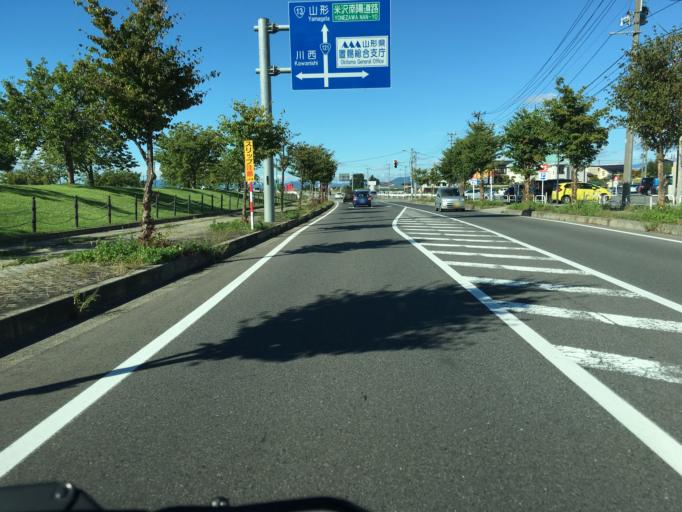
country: JP
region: Yamagata
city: Yonezawa
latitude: 37.9261
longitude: 140.1078
